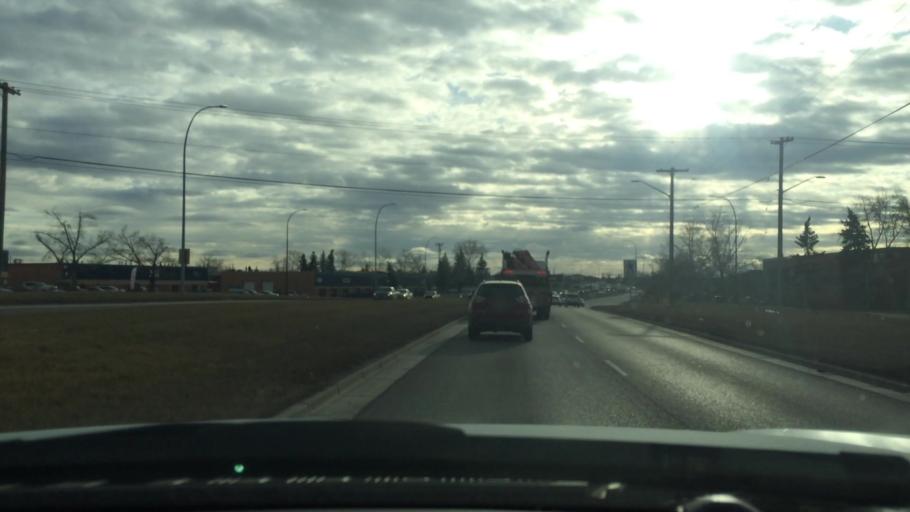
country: CA
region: Alberta
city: Calgary
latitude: 51.0020
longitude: -113.9892
